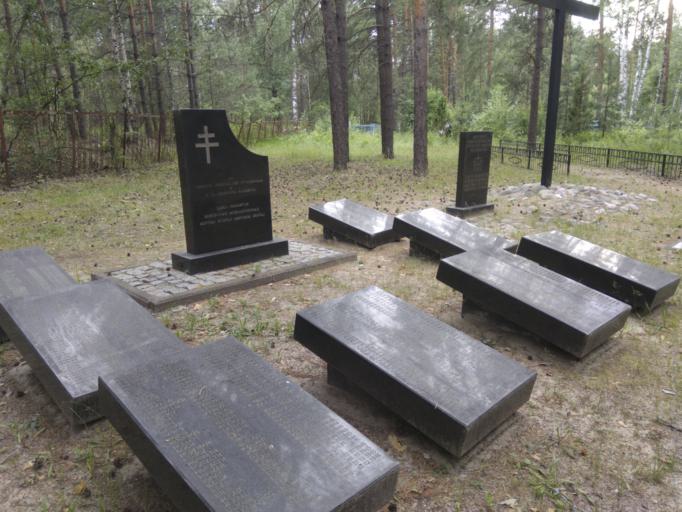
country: RU
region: Ivanovo
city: Talitsy
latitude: 56.5312
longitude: 42.3160
